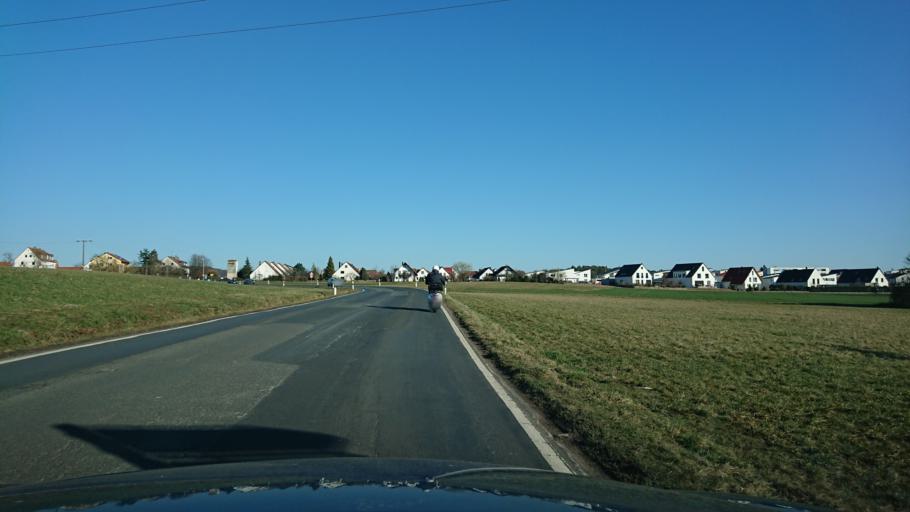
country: DE
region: Bavaria
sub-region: Regierungsbezirk Mittelfranken
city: Spardorf
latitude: 49.6069
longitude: 11.0501
